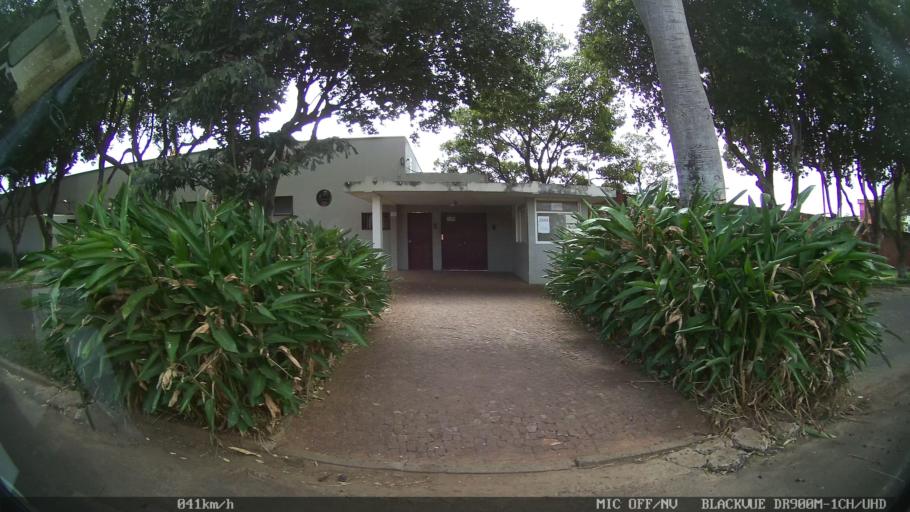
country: BR
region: Sao Paulo
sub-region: Bady Bassitt
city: Bady Bassitt
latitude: -20.8100
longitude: -49.5042
